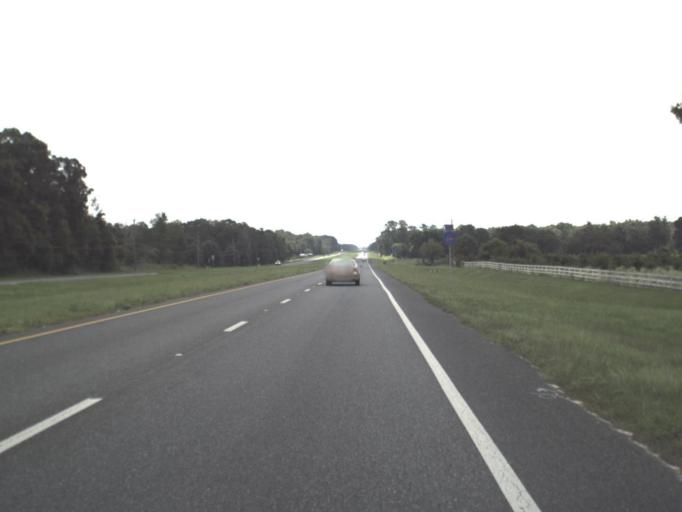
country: US
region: Florida
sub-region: Levy County
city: Williston Highlands
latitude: 29.4069
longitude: -82.5273
